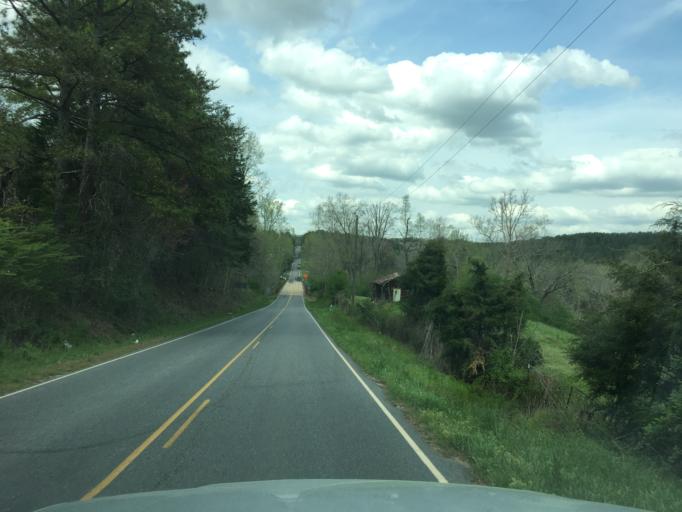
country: US
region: North Carolina
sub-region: Rutherford County
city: Spindale
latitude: 35.2476
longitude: -81.9644
